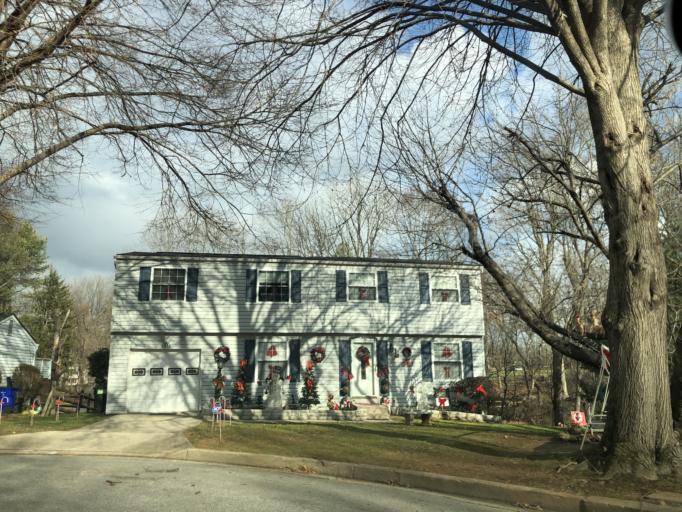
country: US
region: Maryland
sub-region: Howard County
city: Columbia
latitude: 39.1921
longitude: -76.8294
